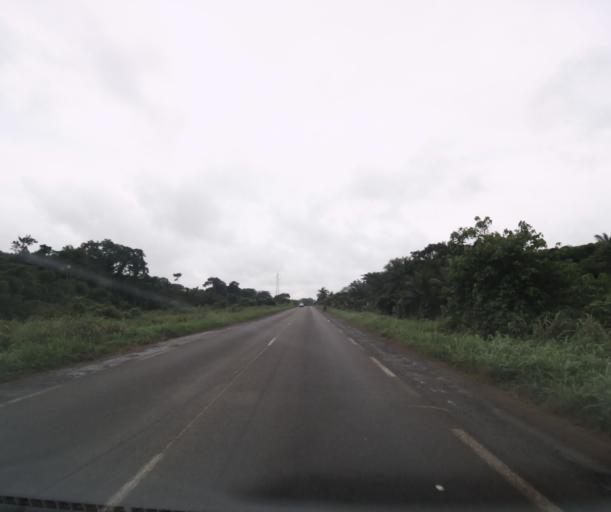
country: CM
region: Littoral
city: Edea
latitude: 3.8355
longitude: 10.4142
